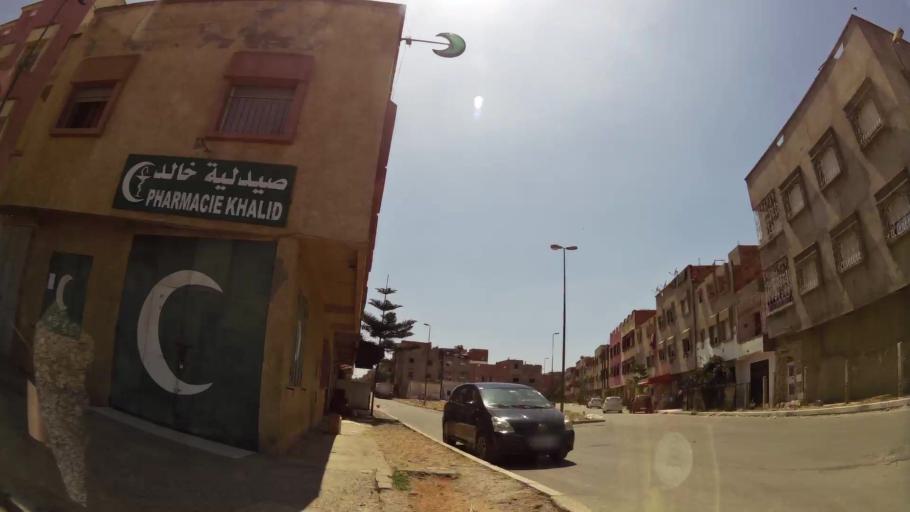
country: MA
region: Gharb-Chrarda-Beni Hssen
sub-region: Kenitra Province
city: Kenitra
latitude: 34.2495
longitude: -6.5377
